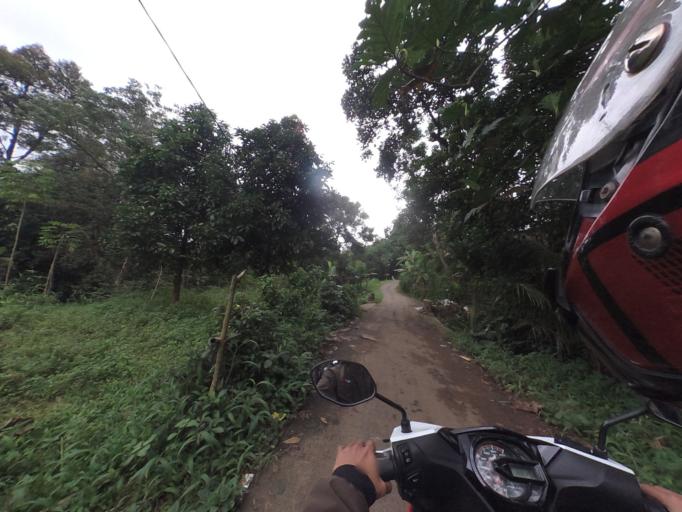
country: ID
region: West Java
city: Bogor
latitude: -6.6145
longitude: 106.7379
